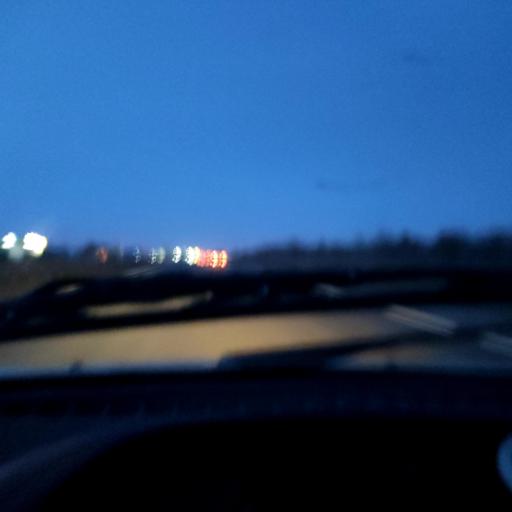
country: RU
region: Samara
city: Tol'yatti
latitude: 53.5676
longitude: 49.3756
